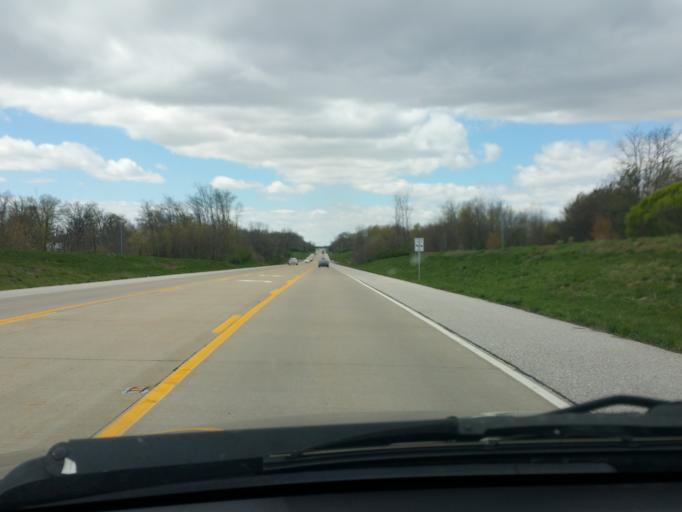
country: US
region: Illinois
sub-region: Madison County
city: Edwardsville
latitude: 38.7873
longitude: -89.9295
